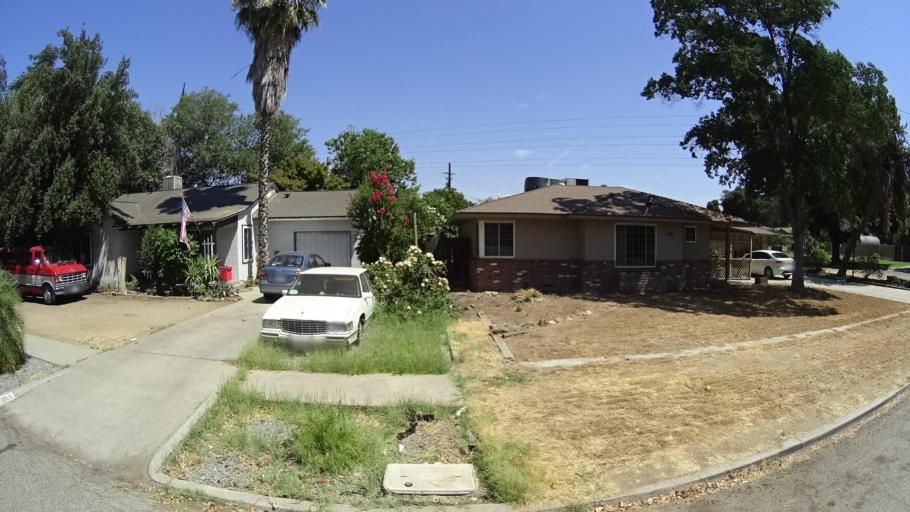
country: US
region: California
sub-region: Fresno County
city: Sunnyside
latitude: 36.7559
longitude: -119.7233
